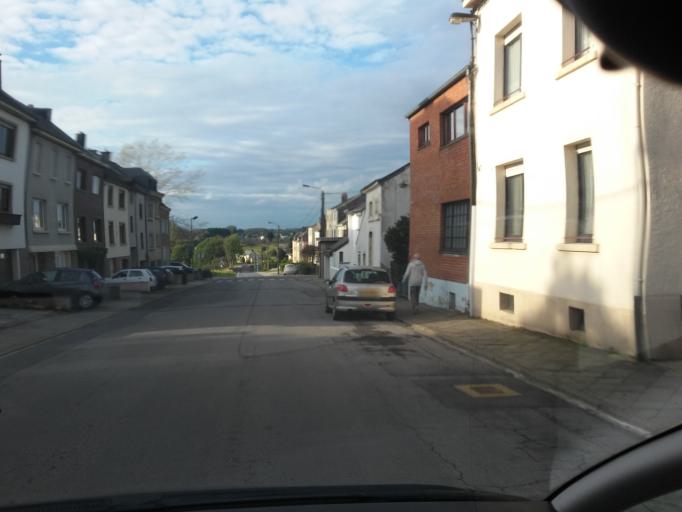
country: BE
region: Wallonia
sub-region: Province du Luxembourg
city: Arlon
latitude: 49.6916
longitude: 5.8039
